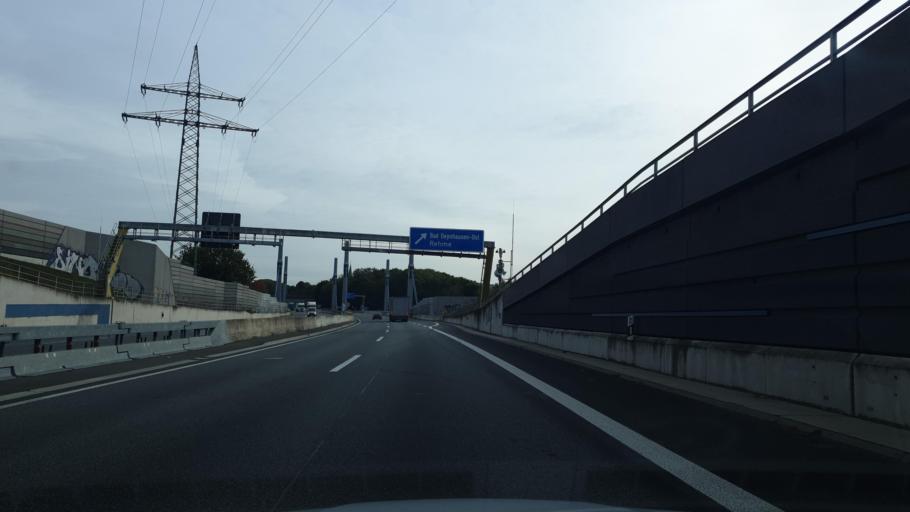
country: DE
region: North Rhine-Westphalia
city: Bad Oeynhausen
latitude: 52.2208
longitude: 8.8227
